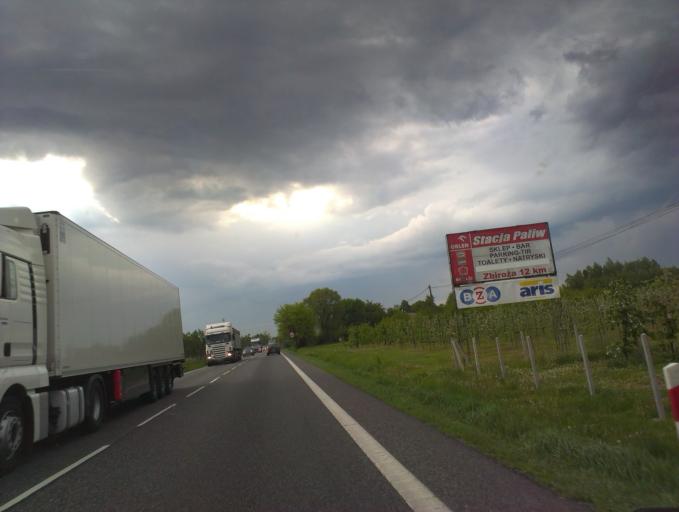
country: PL
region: Masovian Voivodeship
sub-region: Powiat grojecki
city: Pniewy
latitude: 51.9059
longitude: 20.7497
